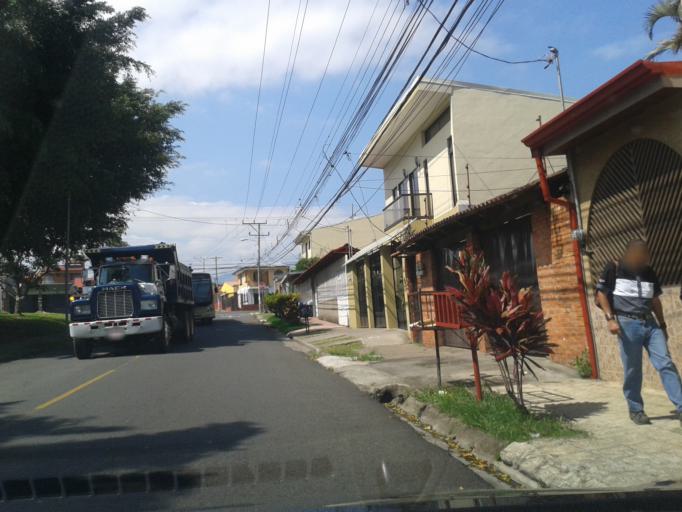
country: CR
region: Heredia
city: San Francisco
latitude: 9.9907
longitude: -84.1400
